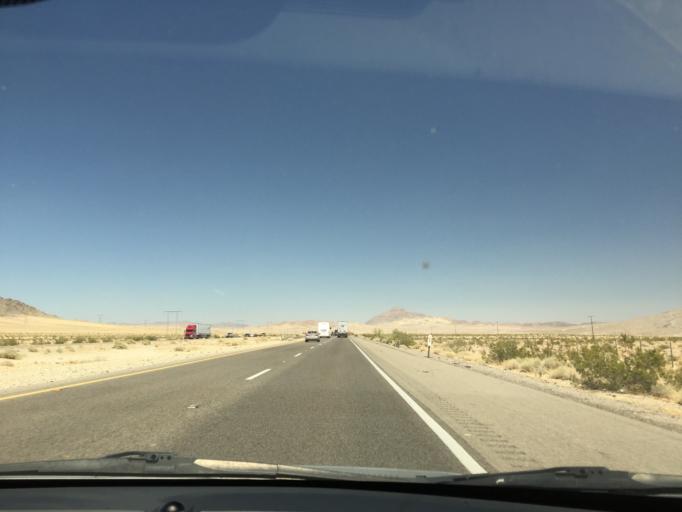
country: US
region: California
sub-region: San Bernardino County
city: Fort Irwin
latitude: 35.0260
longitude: -116.4891
